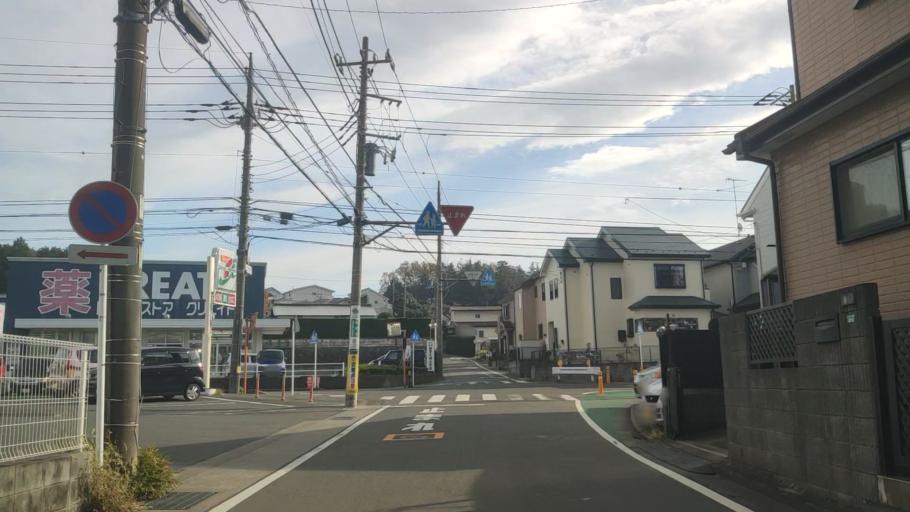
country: JP
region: Kanagawa
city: Atsugi
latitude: 35.4280
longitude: 139.3978
